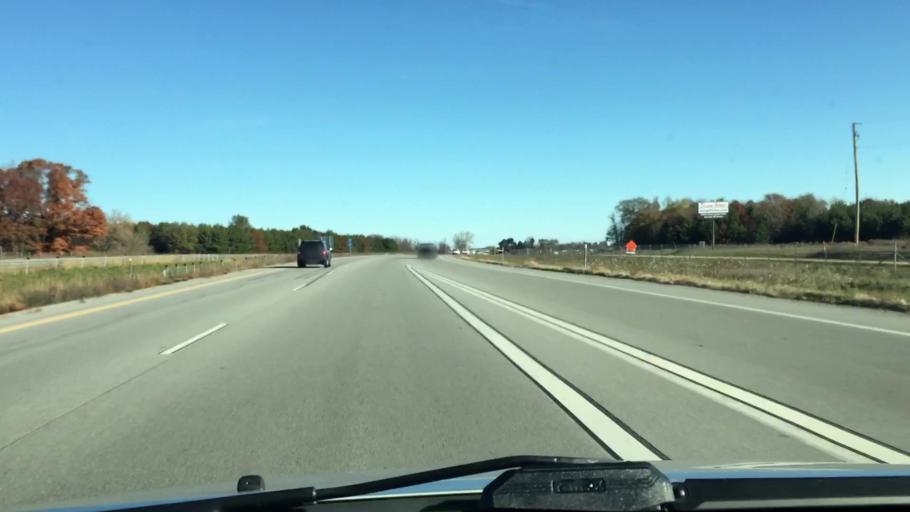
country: US
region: Wisconsin
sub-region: Brown County
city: Wrightstown
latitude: 44.3901
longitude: -88.1604
